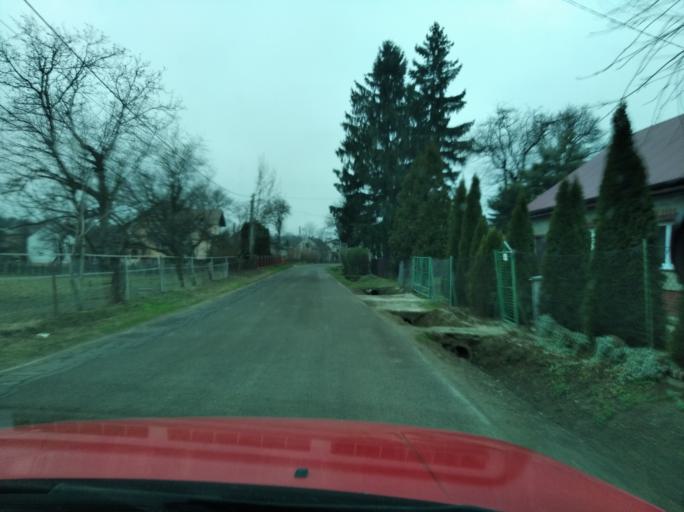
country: PL
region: Subcarpathian Voivodeship
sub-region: Powiat przeworski
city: Mirocin
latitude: 50.0470
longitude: 22.5518
